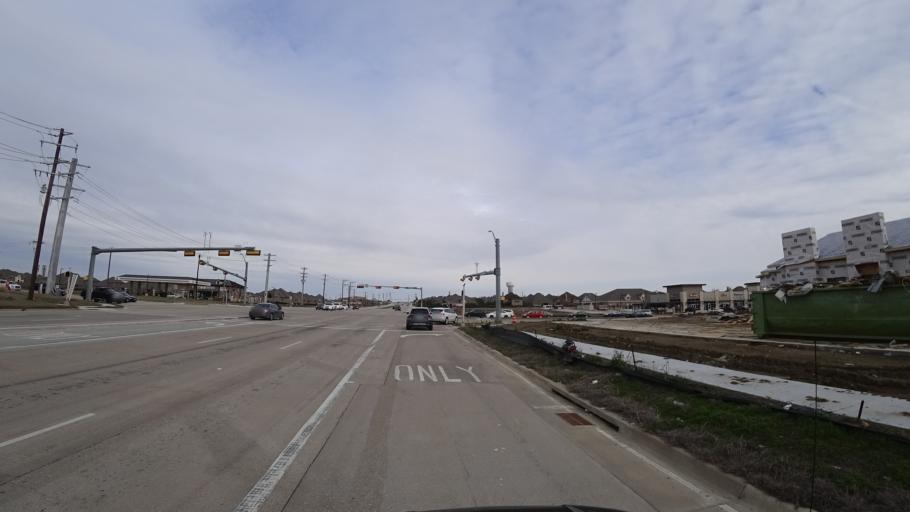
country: US
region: Texas
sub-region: Denton County
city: The Colony
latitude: 33.0462
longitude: -96.9192
